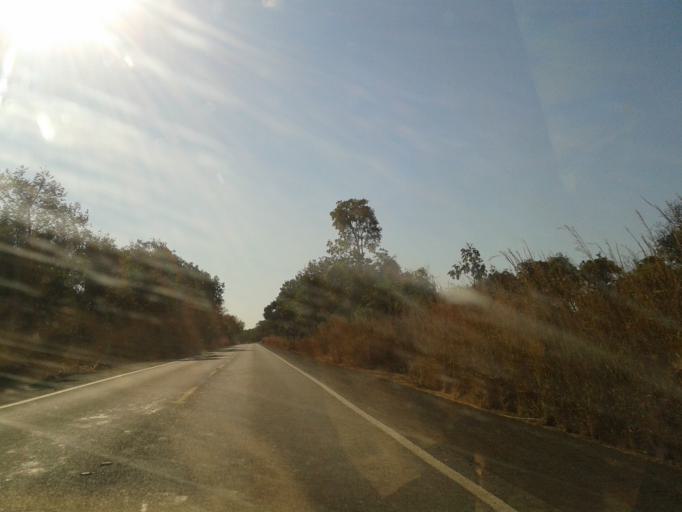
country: BR
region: Goias
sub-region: Mozarlandia
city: Mozarlandia
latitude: -14.9345
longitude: -50.5648
